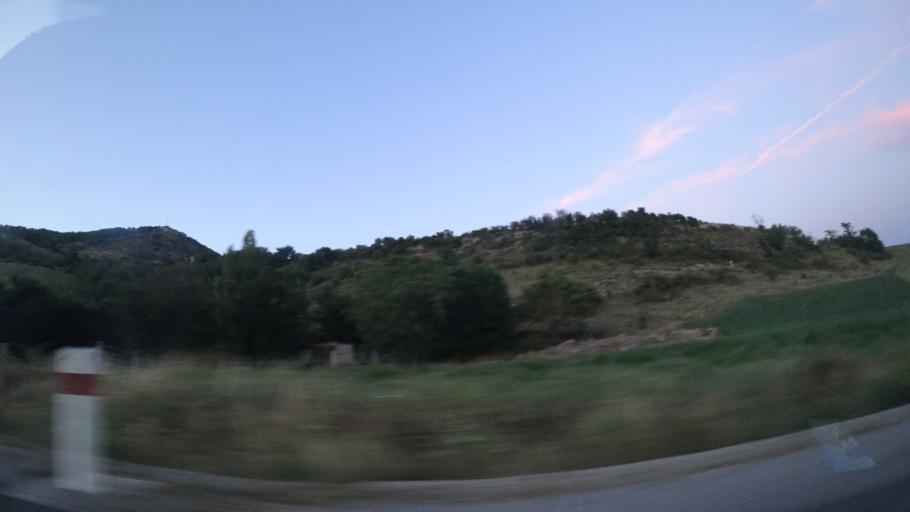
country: FR
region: Midi-Pyrenees
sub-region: Departement de l'Aveyron
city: Millau
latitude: 44.1265
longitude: 3.0562
